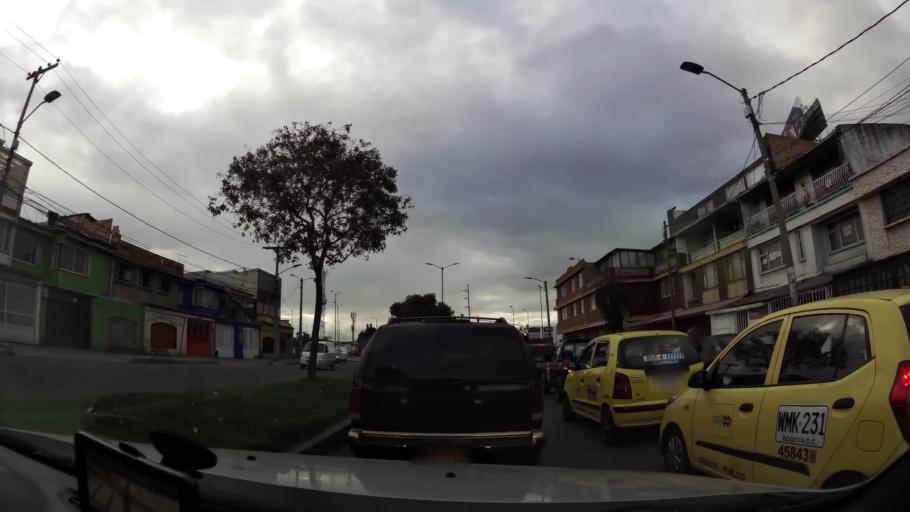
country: CO
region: Bogota D.C.
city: Bogota
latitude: 4.5979
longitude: -74.1064
